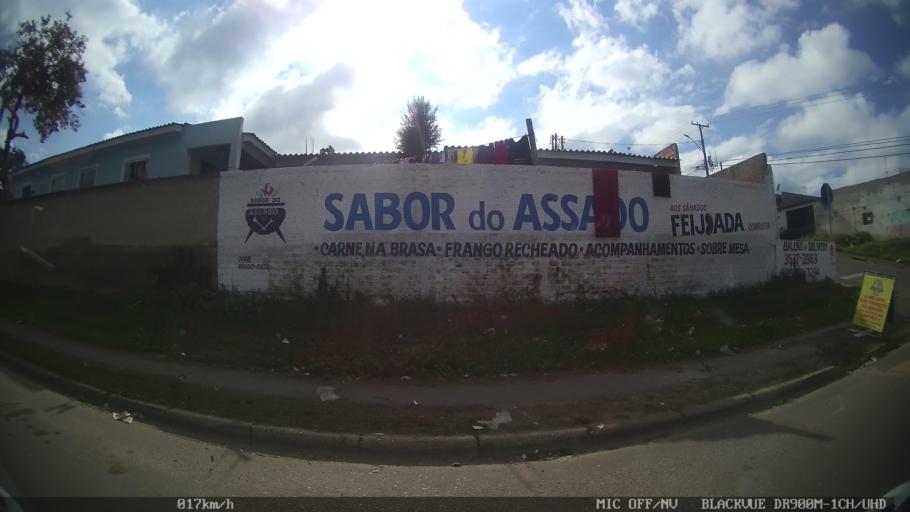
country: BR
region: Parana
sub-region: Colombo
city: Colombo
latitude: -25.3576
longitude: -49.1868
